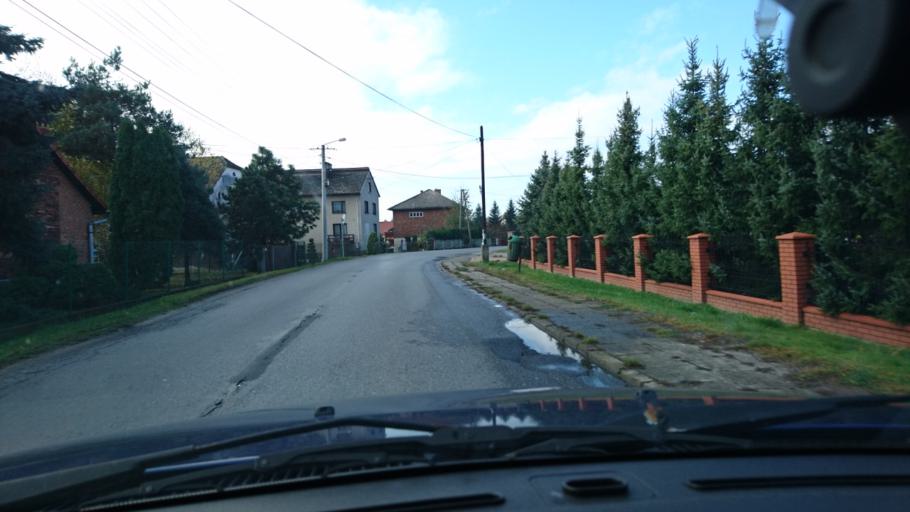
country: PL
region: Lesser Poland Voivodeship
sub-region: Powiat oswiecimski
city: Nowa Wies
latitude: 49.9381
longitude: 19.2075
